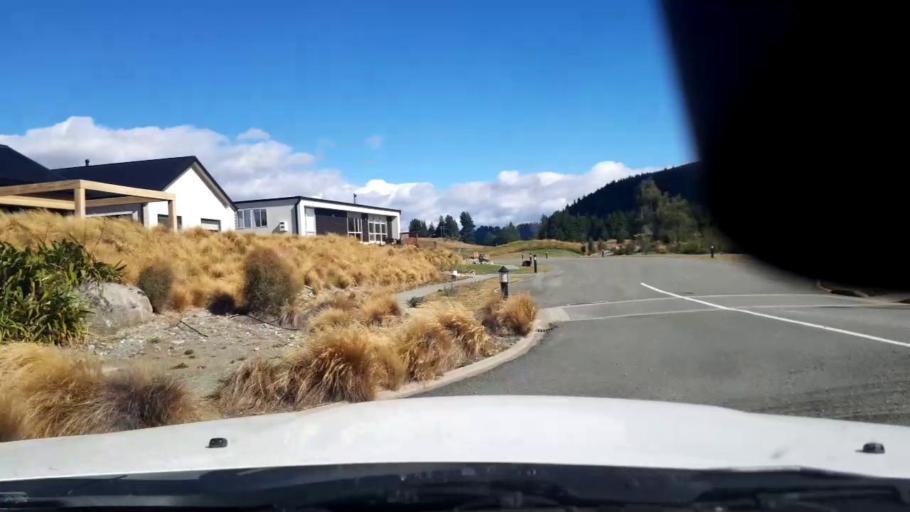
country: NZ
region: Canterbury
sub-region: Timaru District
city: Pleasant Point
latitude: -44.0054
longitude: 170.4719
